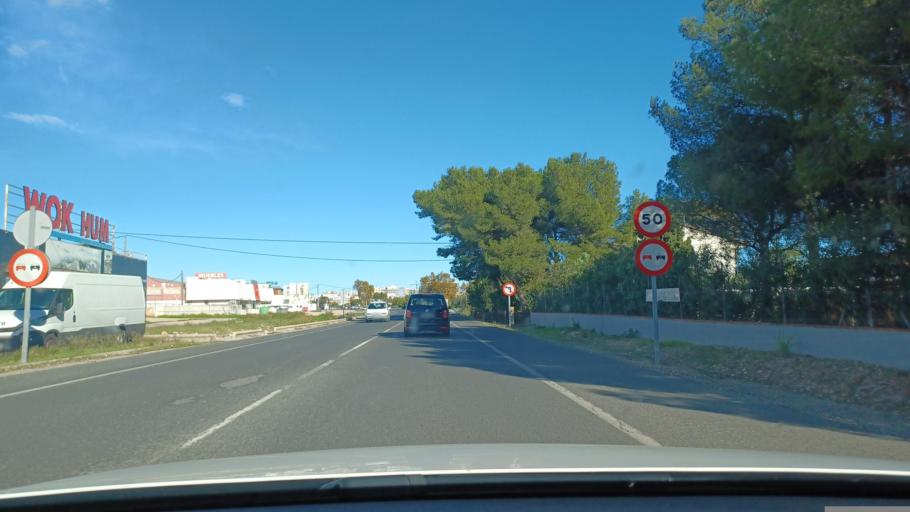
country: ES
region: Valencia
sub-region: Provincia de Castello
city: Vinaros
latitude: 40.4589
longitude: 0.4598
